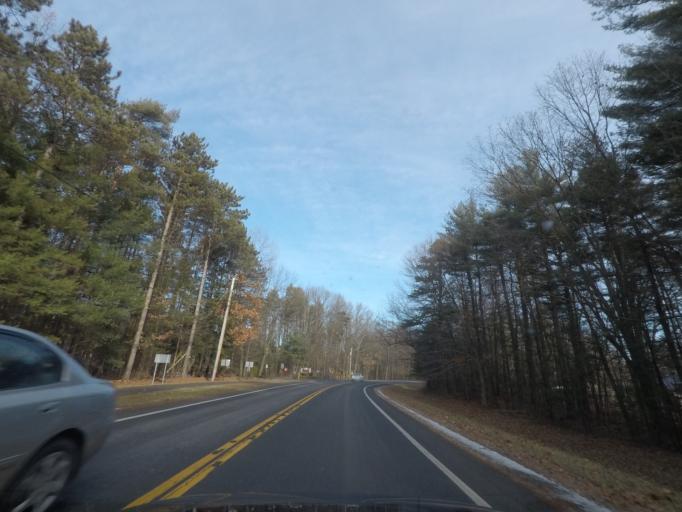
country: US
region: New York
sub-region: Saratoga County
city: Country Knolls
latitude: 42.9744
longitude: -73.7747
